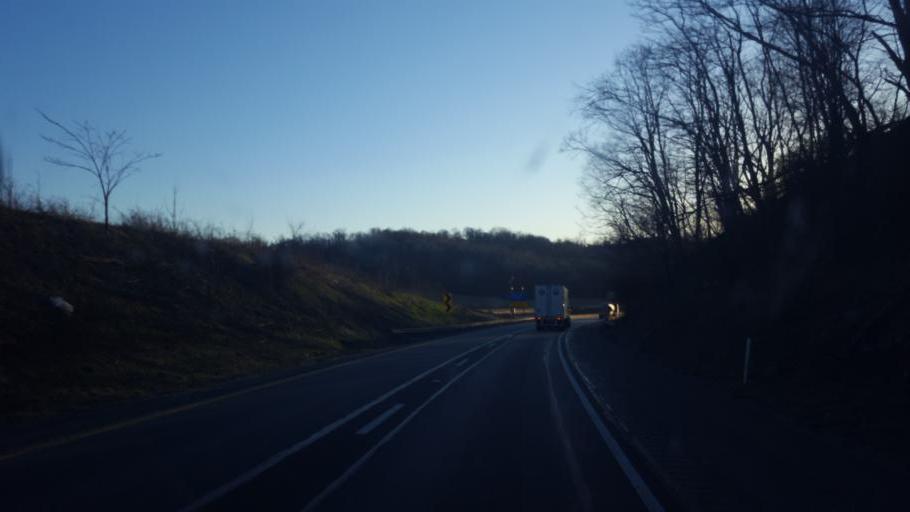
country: US
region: Pennsylvania
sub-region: Washington County
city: Wolfdale
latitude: 40.1250
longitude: -80.3650
